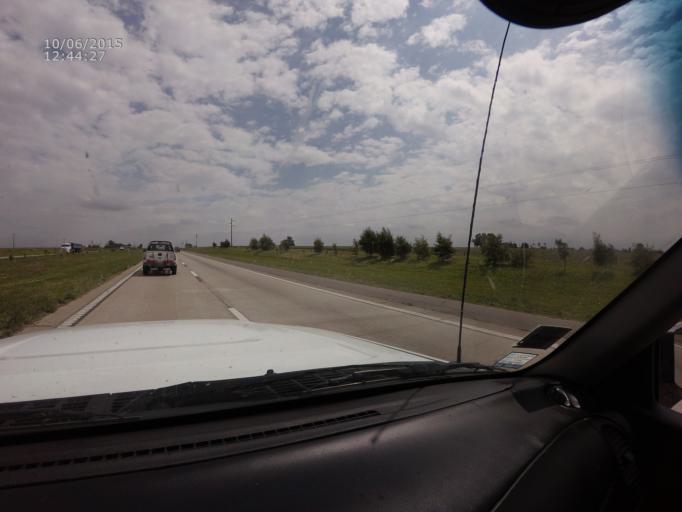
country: AR
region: Santa Fe
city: Canada de Gomez
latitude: -32.8507
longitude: -61.3672
